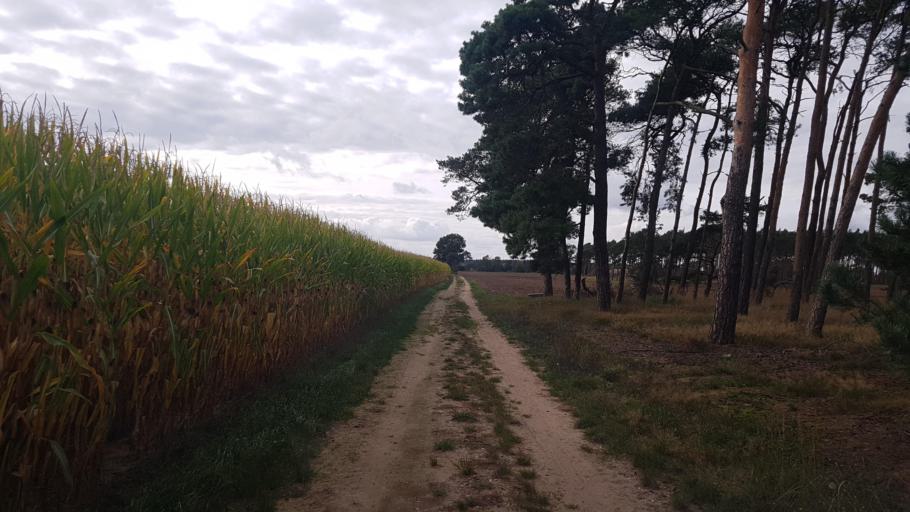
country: DE
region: Brandenburg
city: Bad Liebenwerda
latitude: 51.4744
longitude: 13.4350
